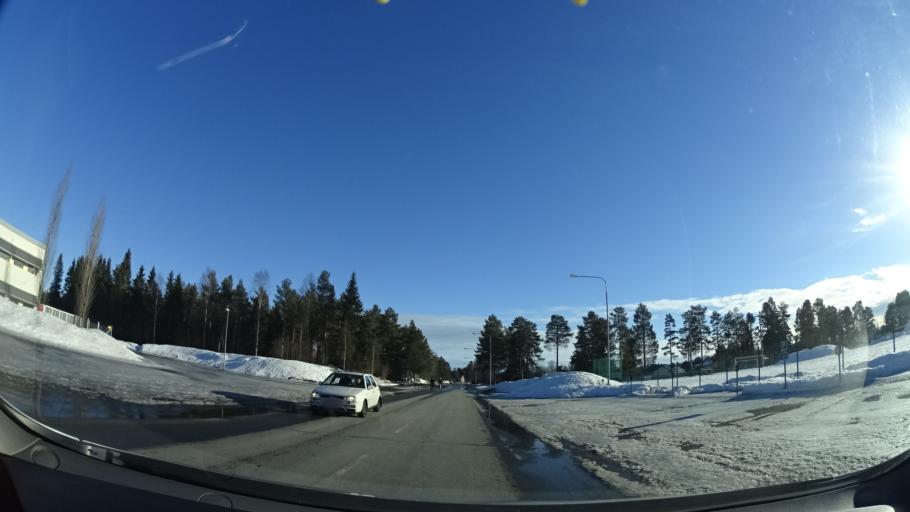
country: SE
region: Vaesterbotten
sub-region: Skelleftea Kommun
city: Byske
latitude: 64.9554
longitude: 21.2113
